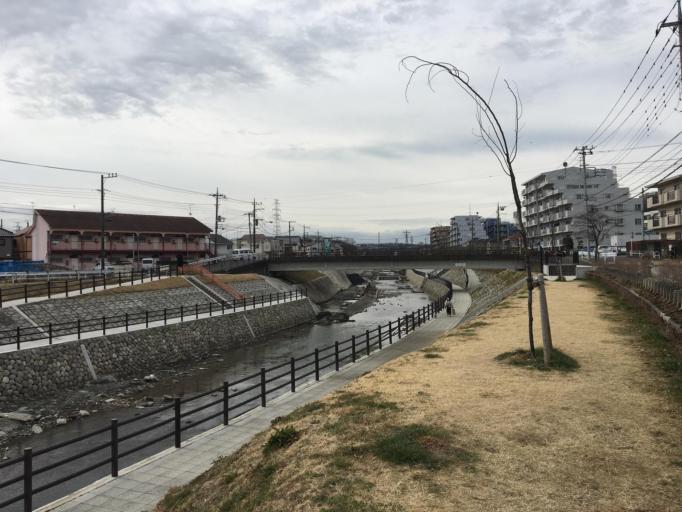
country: JP
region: Tokyo
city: Hino
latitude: 35.6489
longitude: 139.4349
